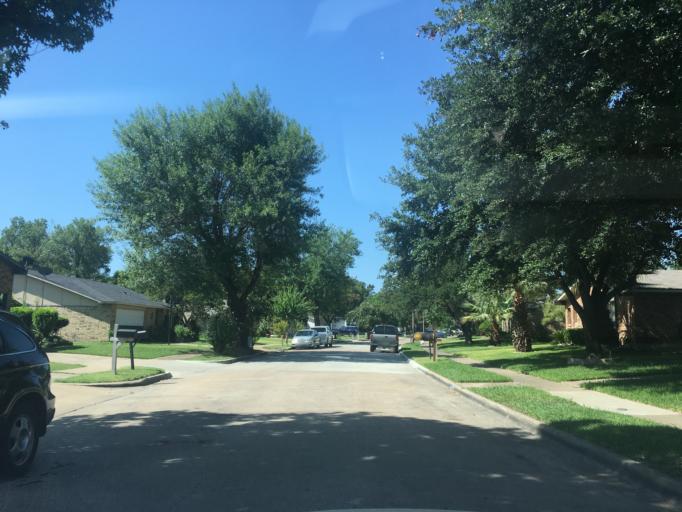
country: US
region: Texas
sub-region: Dallas County
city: Garland
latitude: 32.8545
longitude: -96.6565
